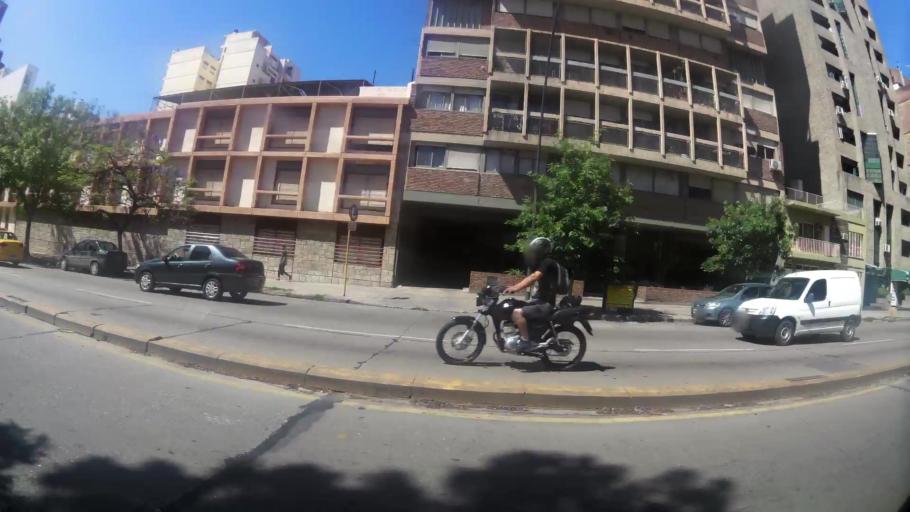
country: AR
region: Cordoba
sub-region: Departamento de Capital
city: Cordoba
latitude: -31.4182
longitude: -64.1920
